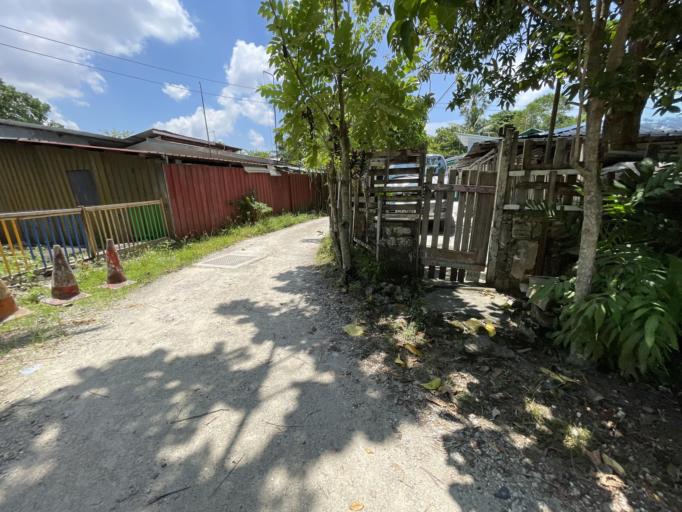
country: MY
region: Johor
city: Kampung Pasir Gudang Baru
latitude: 1.3842
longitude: 103.8789
